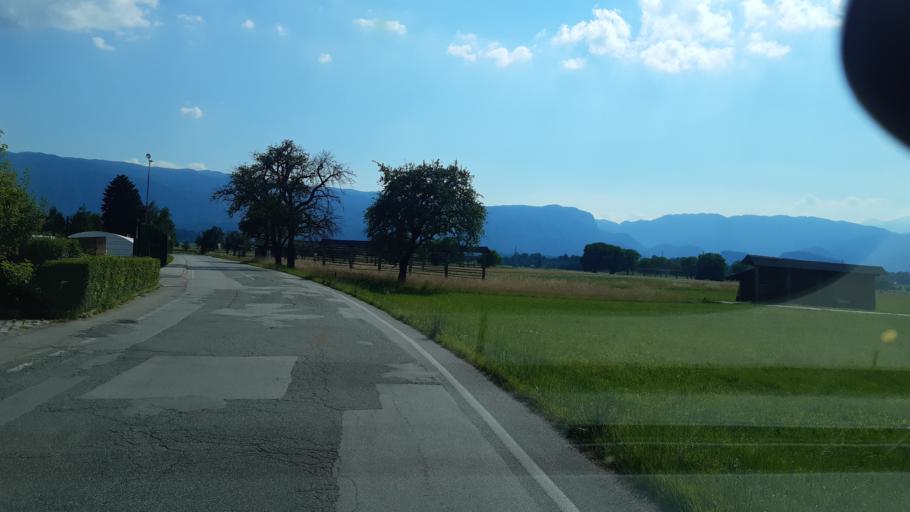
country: SI
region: Radovljica
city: Radovljica
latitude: 46.3713
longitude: 14.1939
